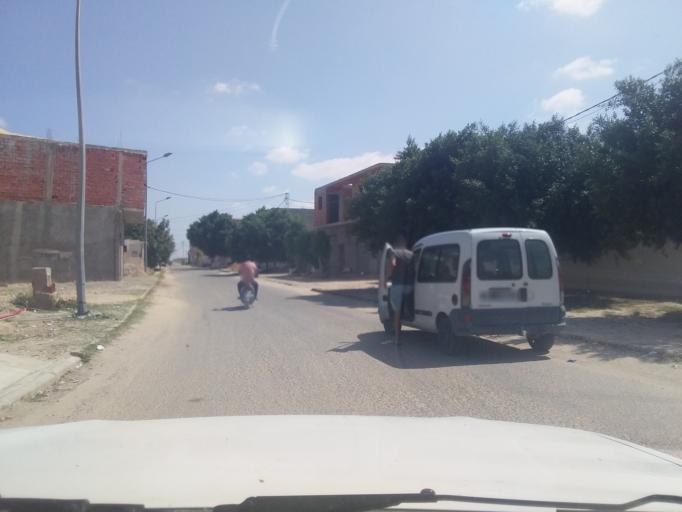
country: TN
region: Qabis
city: Matmata
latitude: 33.6139
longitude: 10.2944
